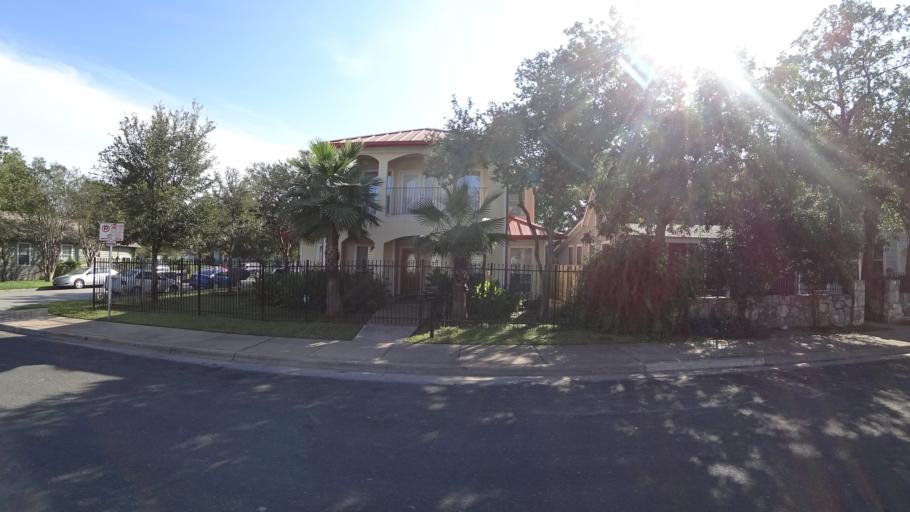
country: US
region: Texas
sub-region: Travis County
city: Austin
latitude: 30.2621
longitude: -97.7329
